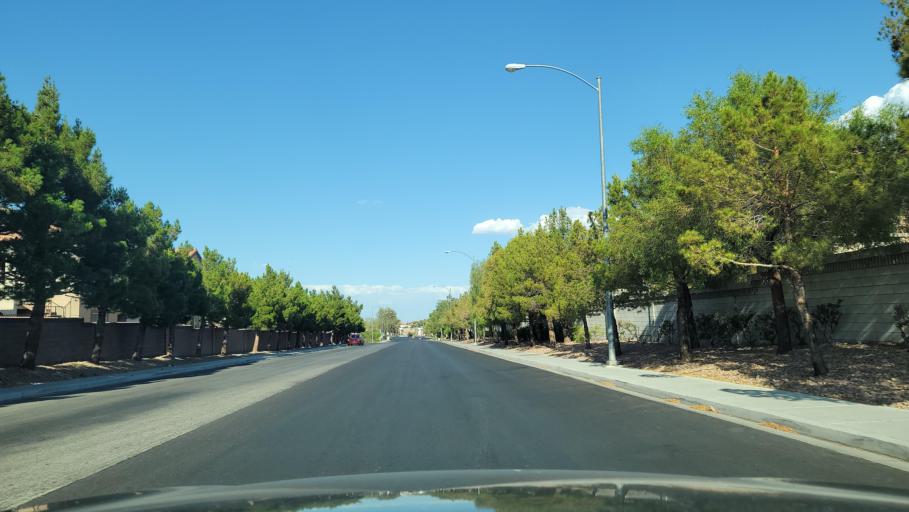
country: US
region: Nevada
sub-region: Clark County
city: Summerlin South
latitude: 36.0963
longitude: -115.3013
